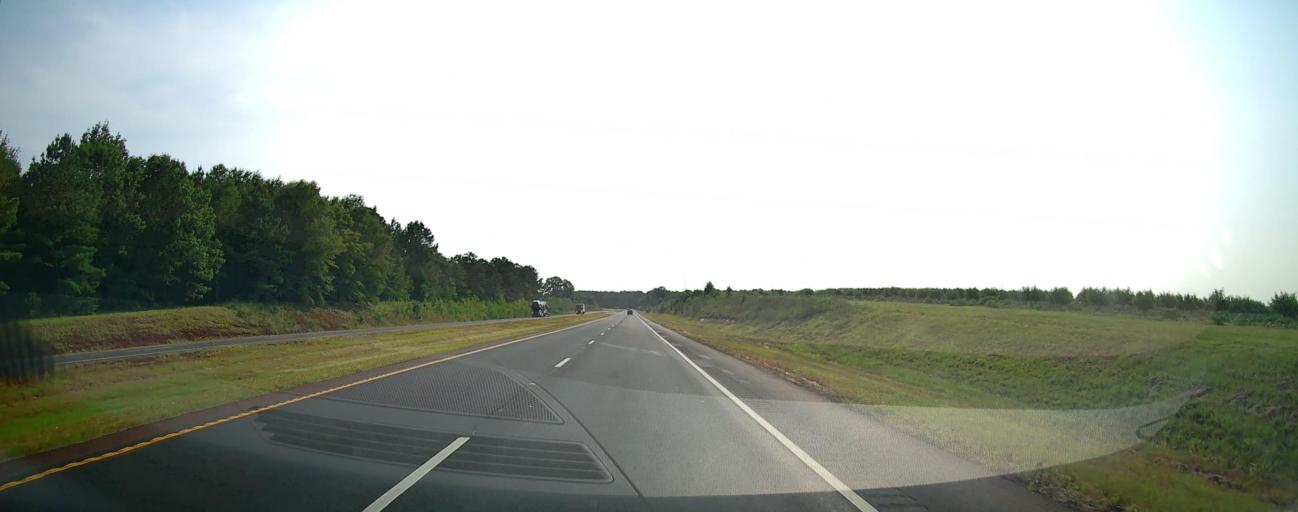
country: US
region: Georgia
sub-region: Peach County
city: Fort Valley
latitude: 32.5701
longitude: -83.9231
